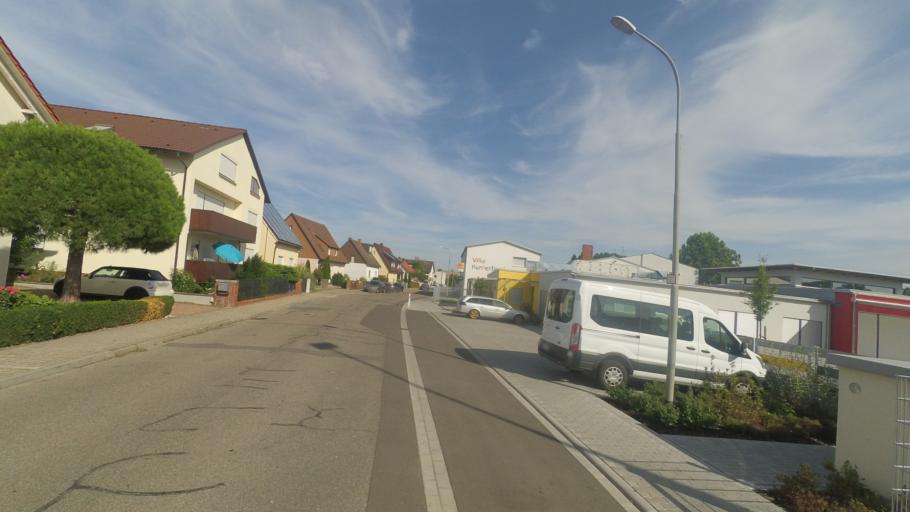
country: DE
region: Rheinland-Pfalz
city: Limburgerhof
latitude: 49.4199
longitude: 8.3830
